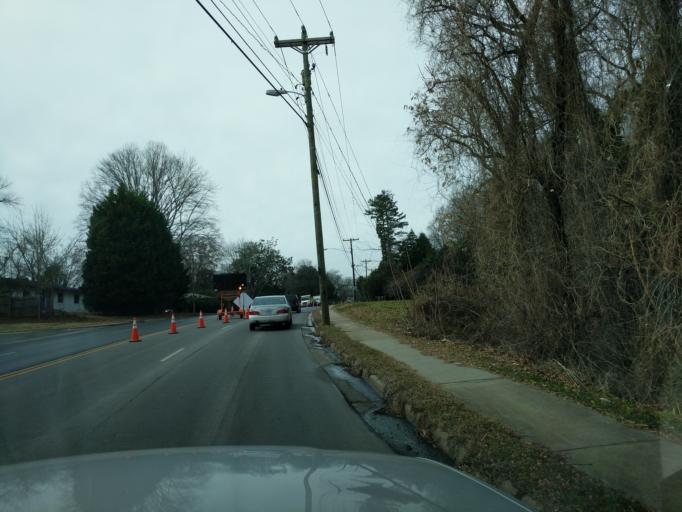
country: US
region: North Carolina
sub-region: Mecklenburg County
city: Charlotte
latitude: 35.1726
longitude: -80.8617
